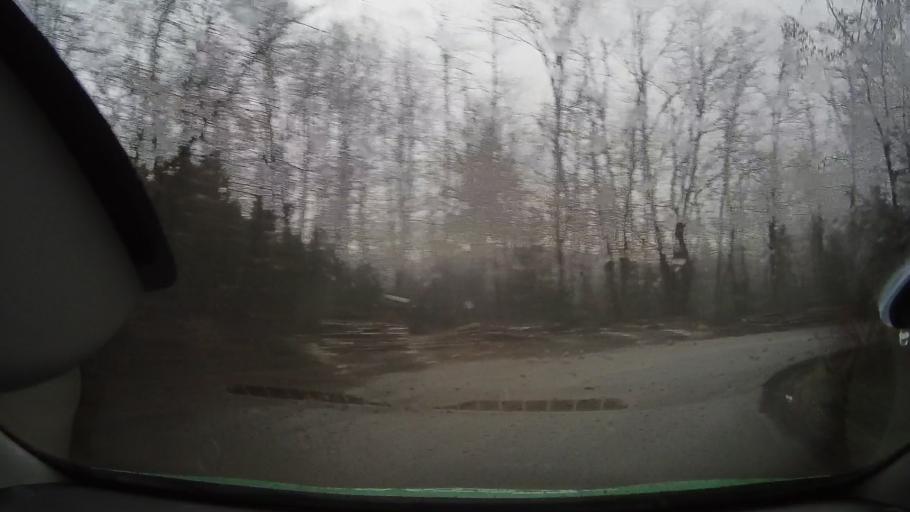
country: RO
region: Hunedoara
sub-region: Comuna Ribita
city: Ribita
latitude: 46.2496
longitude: 22.7461
